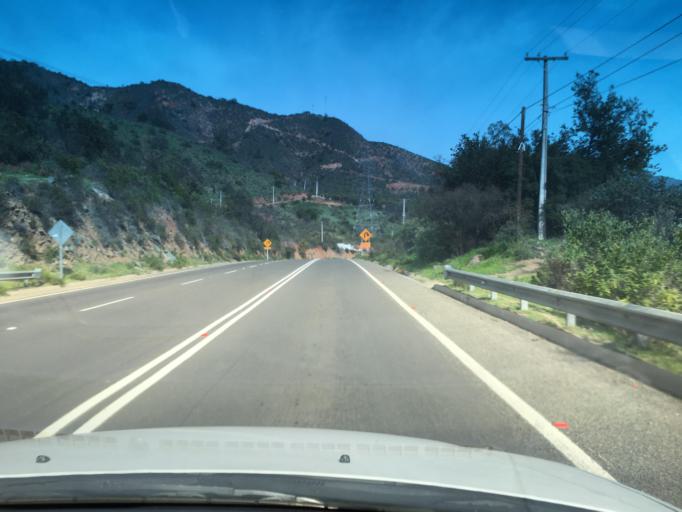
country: CL
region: Valparaiso
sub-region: Provincia de Marga Marga
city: Limache
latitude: -33.0595
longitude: -71.0501
